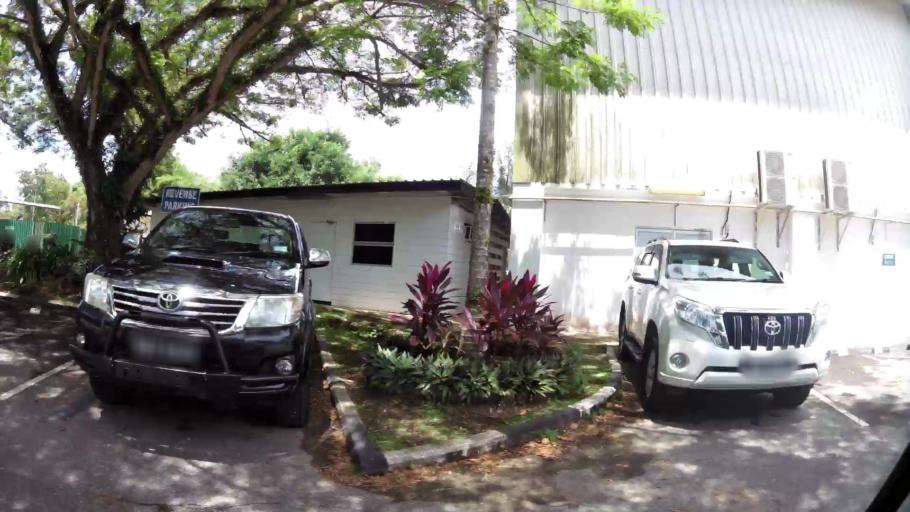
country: BN
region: Belait
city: Kuala Belait
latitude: 4.6006
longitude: 114.2697
